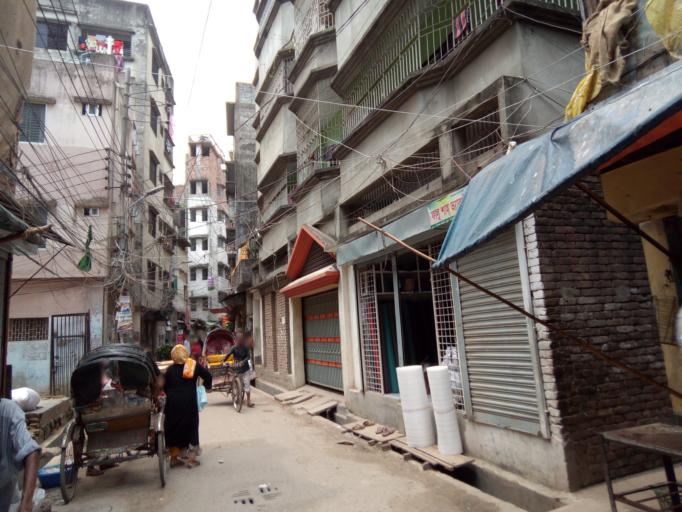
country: BD
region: Dhaka
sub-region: Dhaka
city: Dhaka
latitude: 23.7203
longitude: 90.4014
